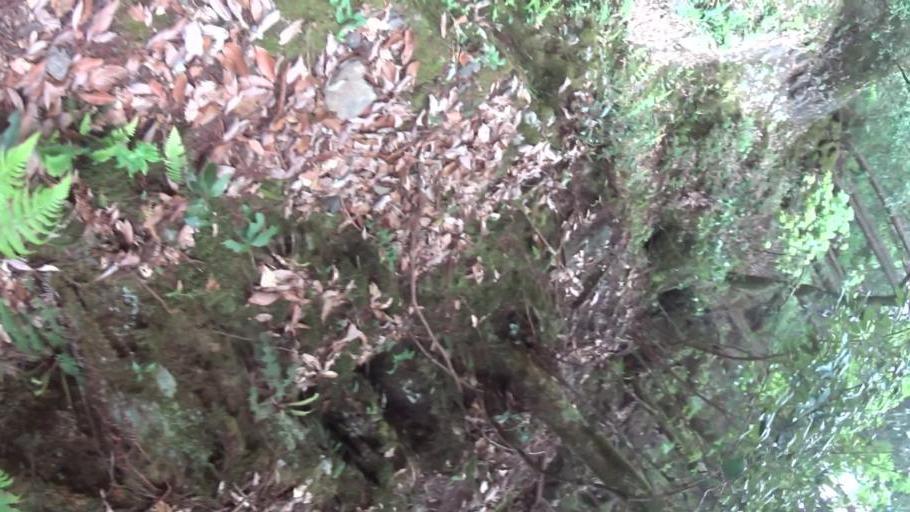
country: JP
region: Kyoto
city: Kameoka
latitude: 35.0351
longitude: 135.6516
